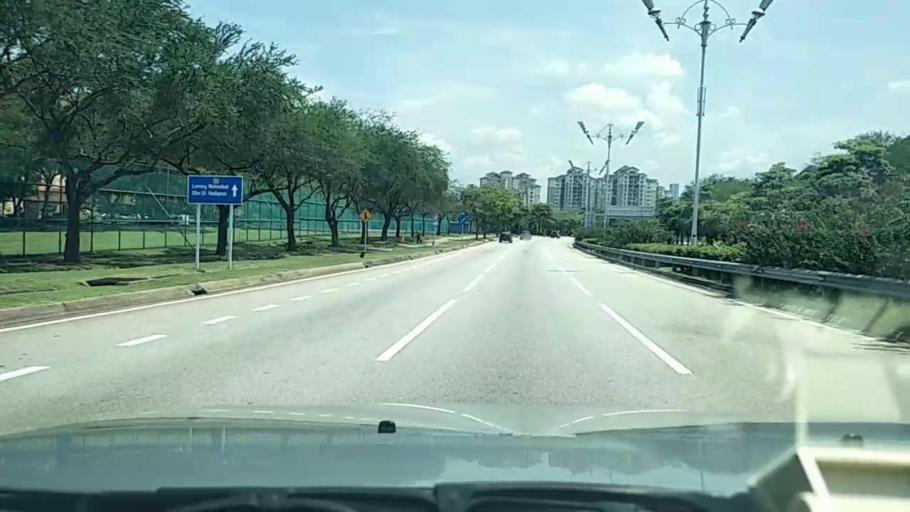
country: MY
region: Putrajaya
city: Putrajaya
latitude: 2.9484
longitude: 101.6812
